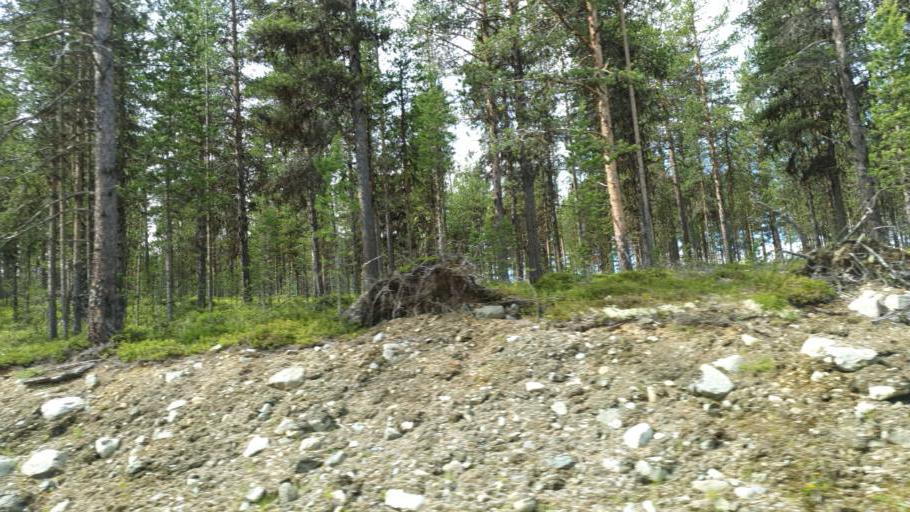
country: NO
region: Oppland
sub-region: Vaga
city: Vagamo
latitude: 61.7064
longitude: 9.0577
